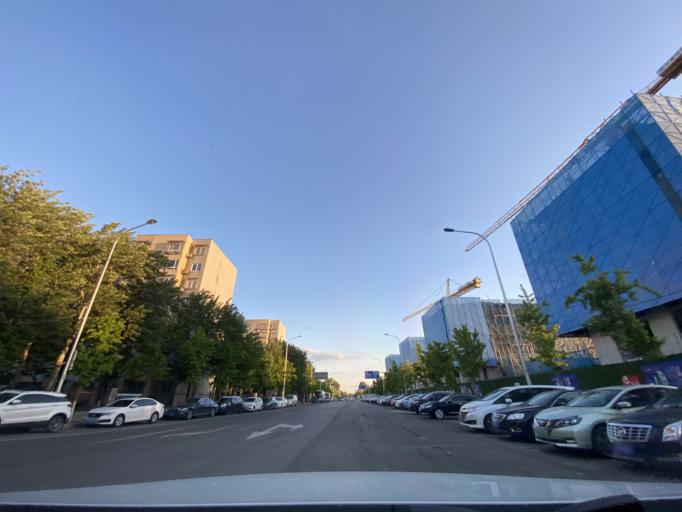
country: CN
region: Beijing
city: Sijiqing
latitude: 39.9547
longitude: 116.2632
